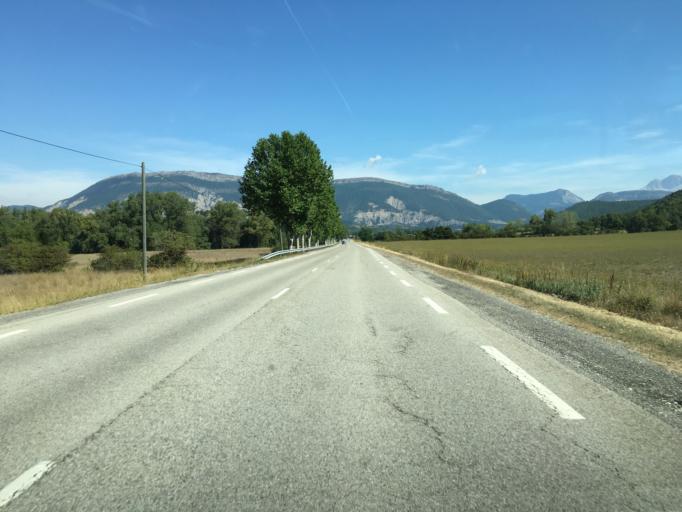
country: FR
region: Provence-Alpes-Cote d'Azur
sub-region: Departement des Hautes-Alpes
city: Serres
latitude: 44.4781
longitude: 5.7272
